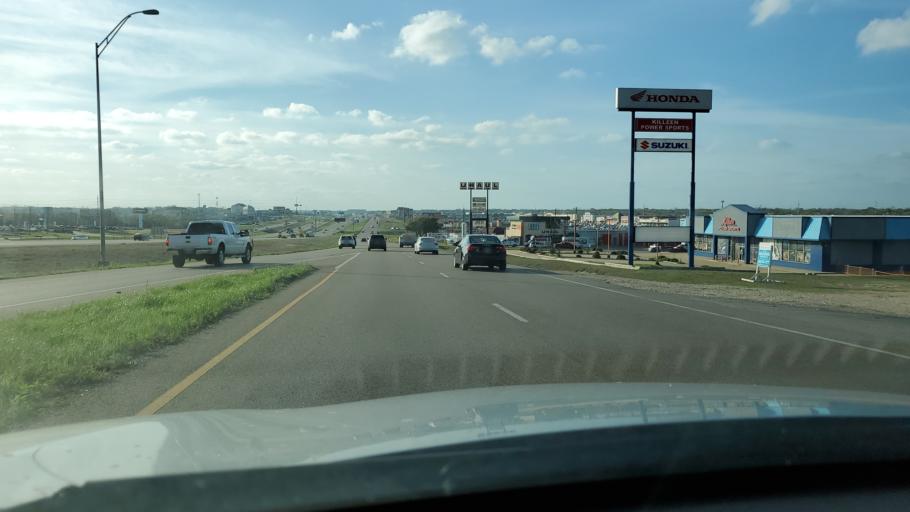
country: US
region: Texas
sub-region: Bell County
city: Harker Heights
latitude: 31.0826
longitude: -97.7018
